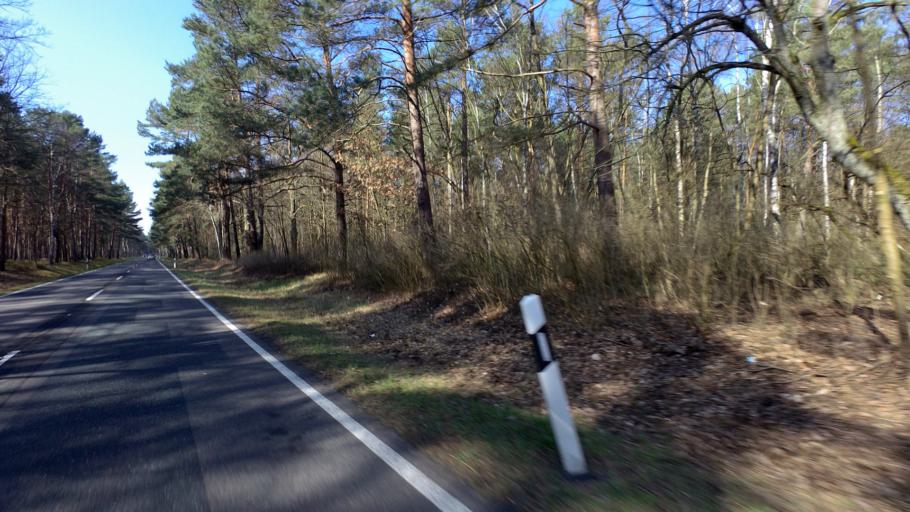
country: DE
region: Brandenburg
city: Sperenberg
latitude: 52.0889
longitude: 13.3349
